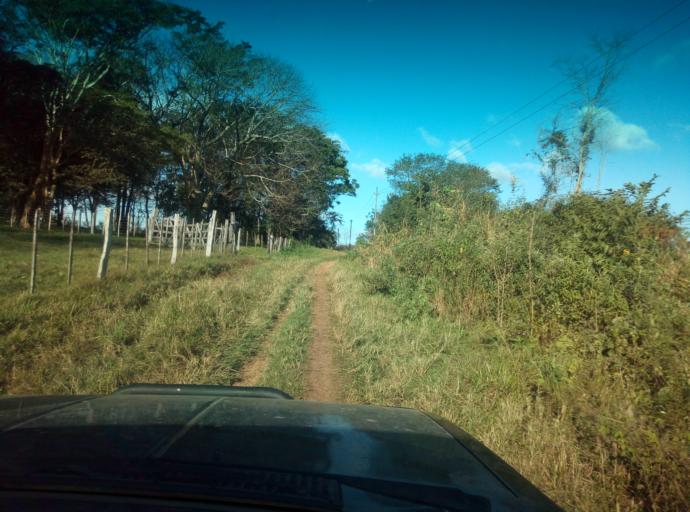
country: PY
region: Caaguazu
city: Carayao
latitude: -25.1820
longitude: -56.2661
